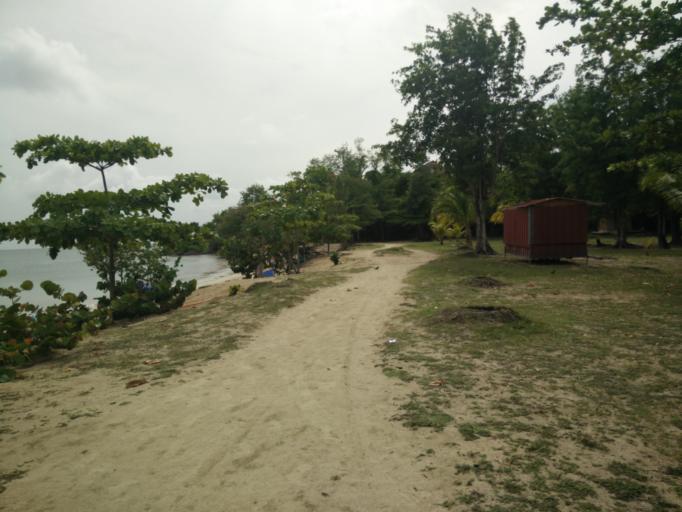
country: MQ
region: Martinique
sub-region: Martinique
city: Sainte-Luce
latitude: 14.4683
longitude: -60.9577
